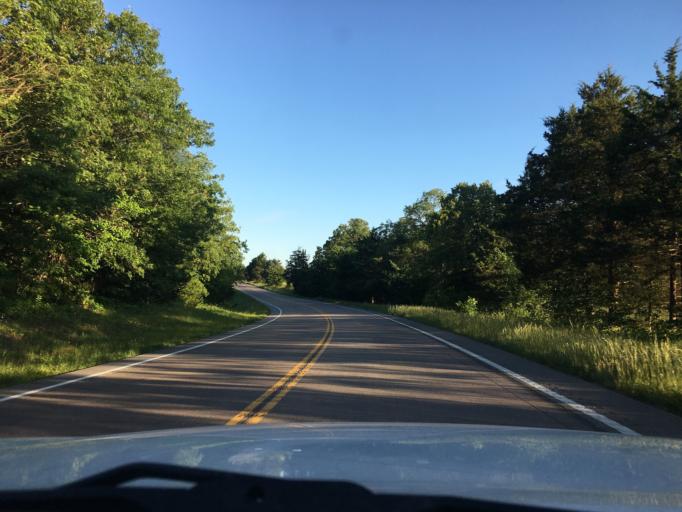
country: US
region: Missouri
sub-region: Gasconade County
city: Owensville
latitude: 38.4506
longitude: -91.4481
